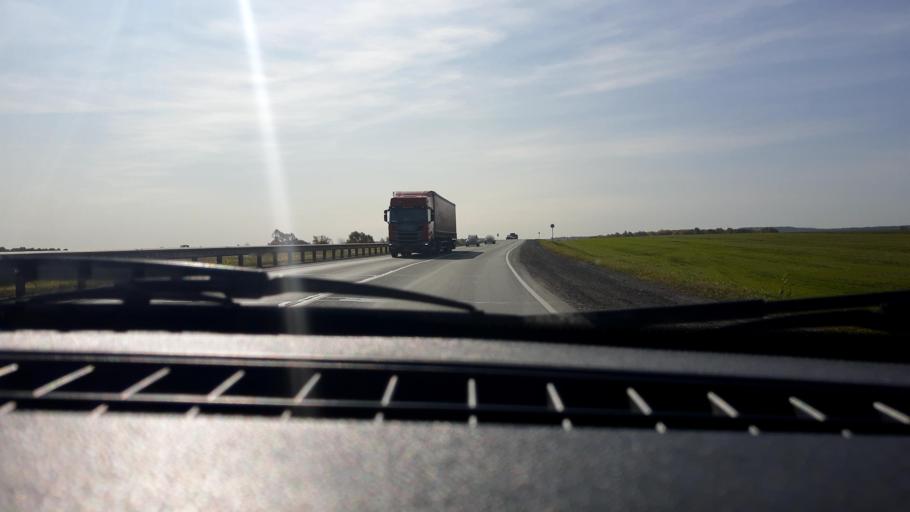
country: RU
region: Bashkortostan
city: Mikhaylovka
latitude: 54.7741
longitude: 55.7858
